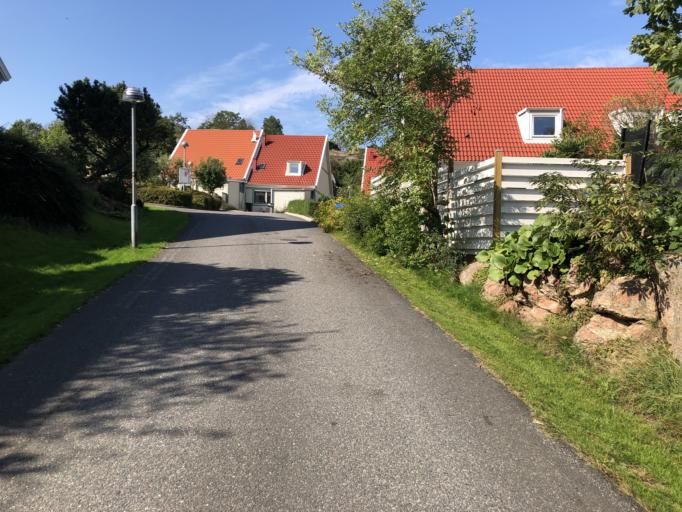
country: SE
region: Vaestra Goetaland
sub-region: Goteborg
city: Goeteborg
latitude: 57.7420
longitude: 11.9661
